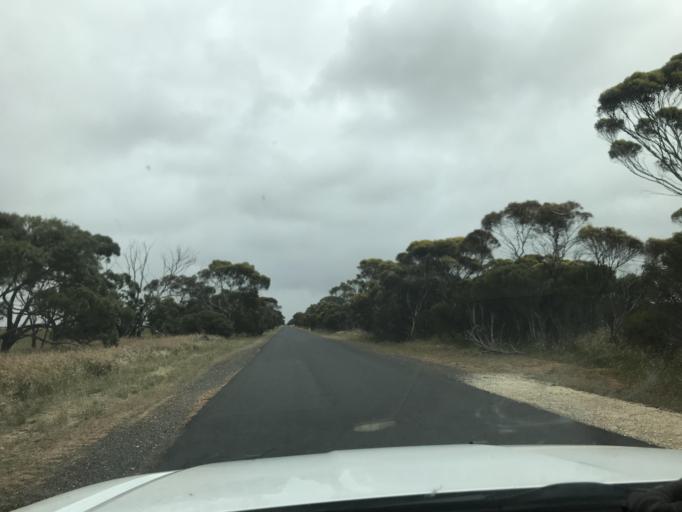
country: AU
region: South Australia
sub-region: Tatiara
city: Bordertown
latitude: -36.1202
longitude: 141.0613
